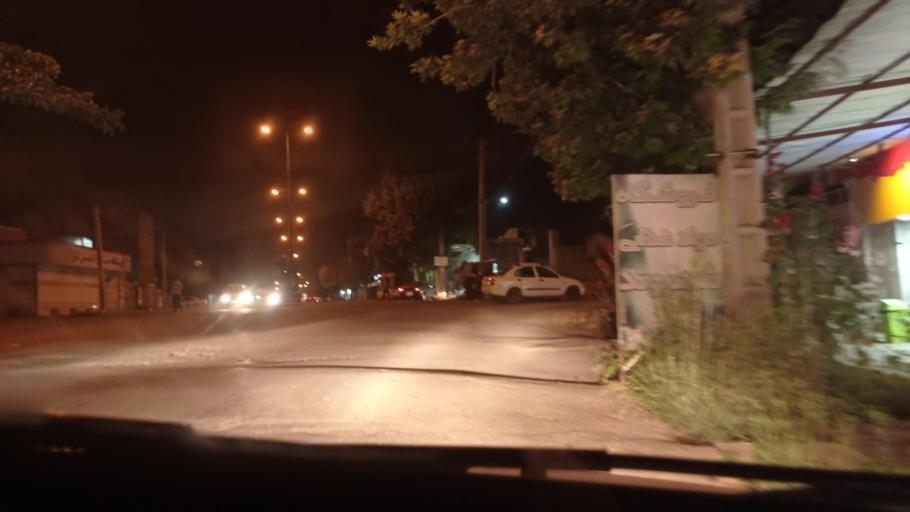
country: IR
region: Lorestan
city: Kuhdasht
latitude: 33.5390
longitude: 47.6074
